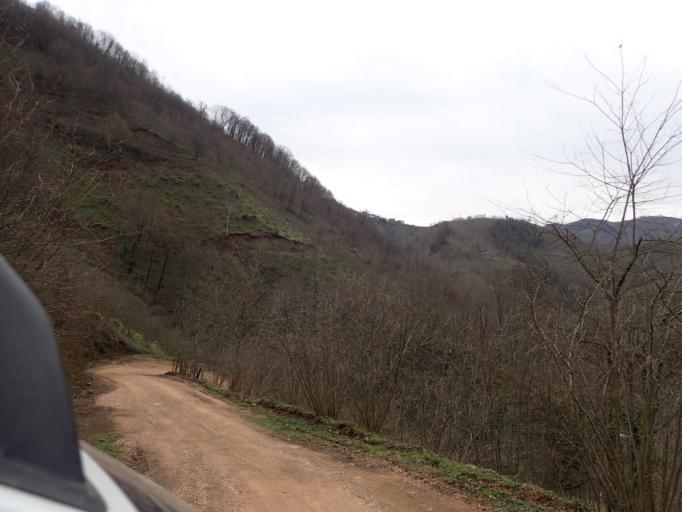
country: TR
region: Ordu
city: Camas
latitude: 40.8887
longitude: 37.5091
